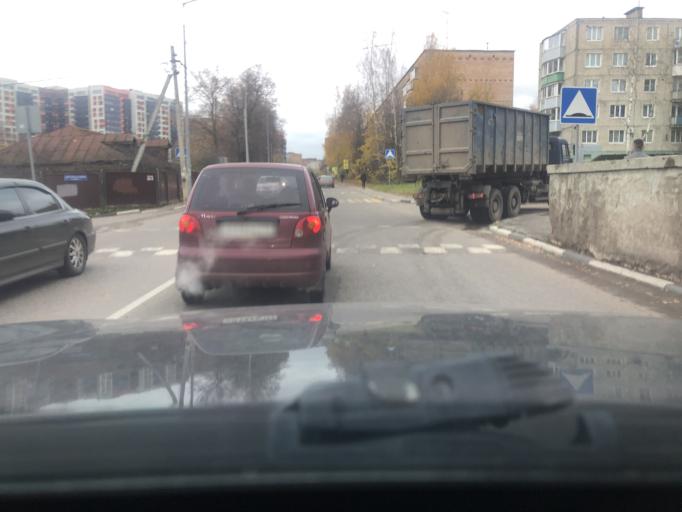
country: RU
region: Moskovskaya
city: Sergiyev Posad
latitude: 56.3208
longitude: 38.1320
